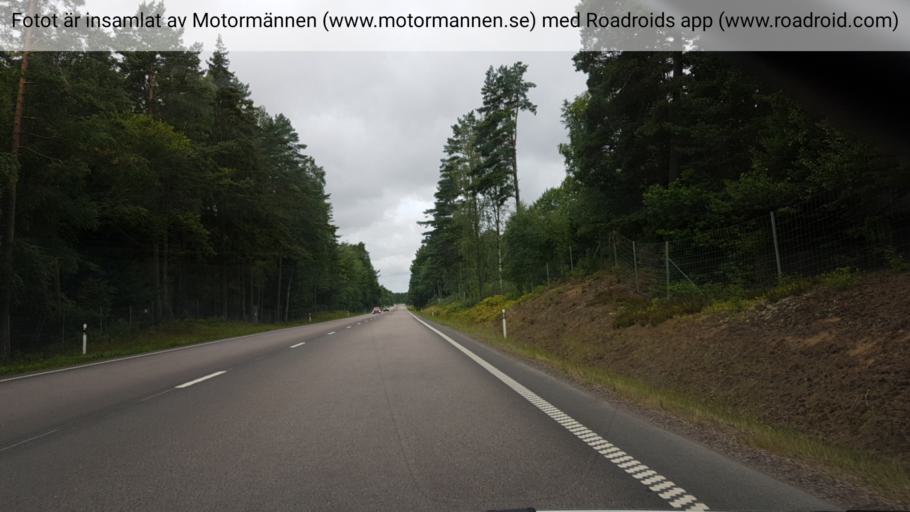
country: SE
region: Vaestra Goetaland
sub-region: Lidkopings Kommun
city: Vinninga
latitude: 58.4291
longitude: 13.3151
